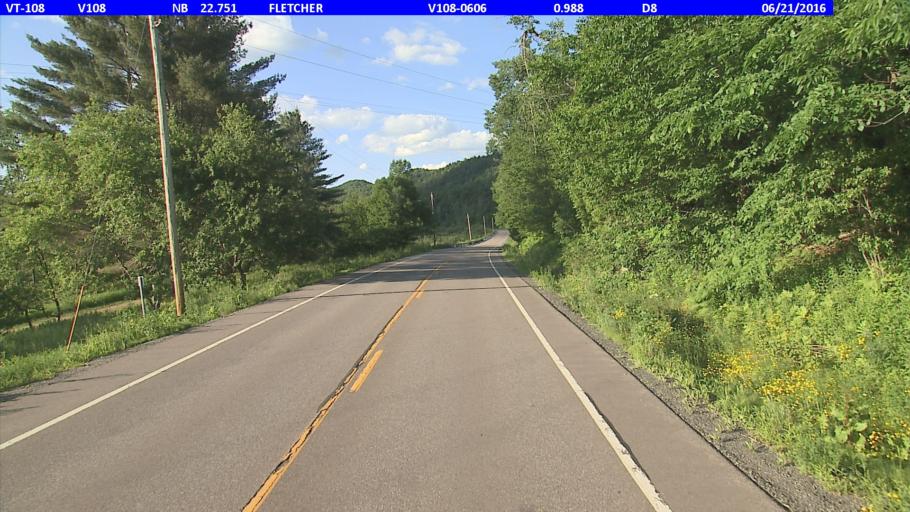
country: US
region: Vermont
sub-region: Lamoille County
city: Johnson
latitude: 44.7156
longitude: -72.8358
